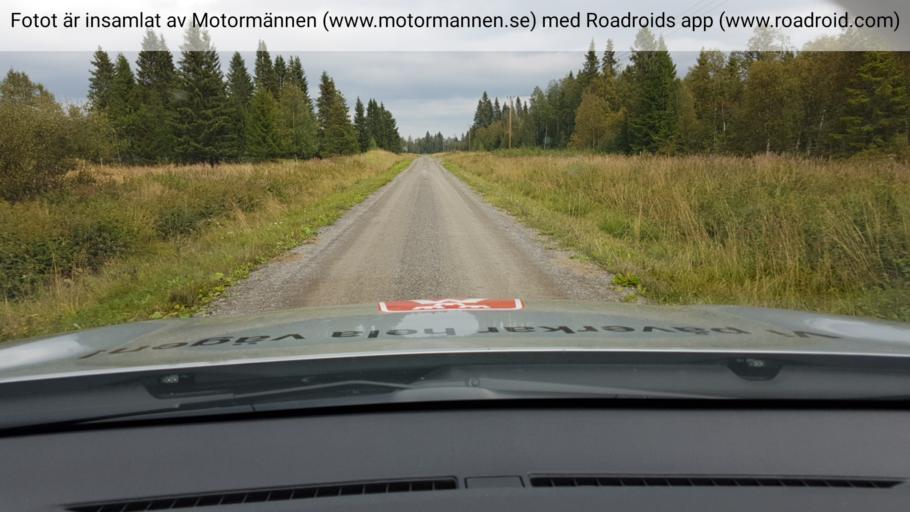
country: SE
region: Jaemtland
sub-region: Stroemsunds Kommun
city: Stroemsund
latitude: 63.7796
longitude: 15.2414
